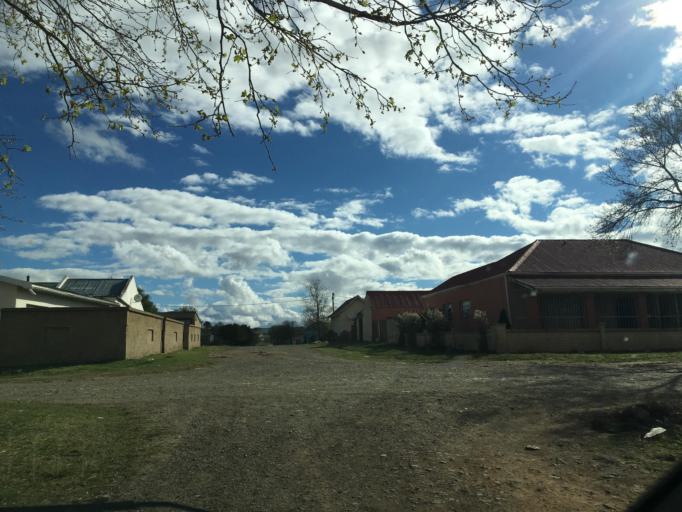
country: ZA
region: Eastern Cape
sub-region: Chris Hani District Municipality
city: Elliot
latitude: -31.3355
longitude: 27.8521
